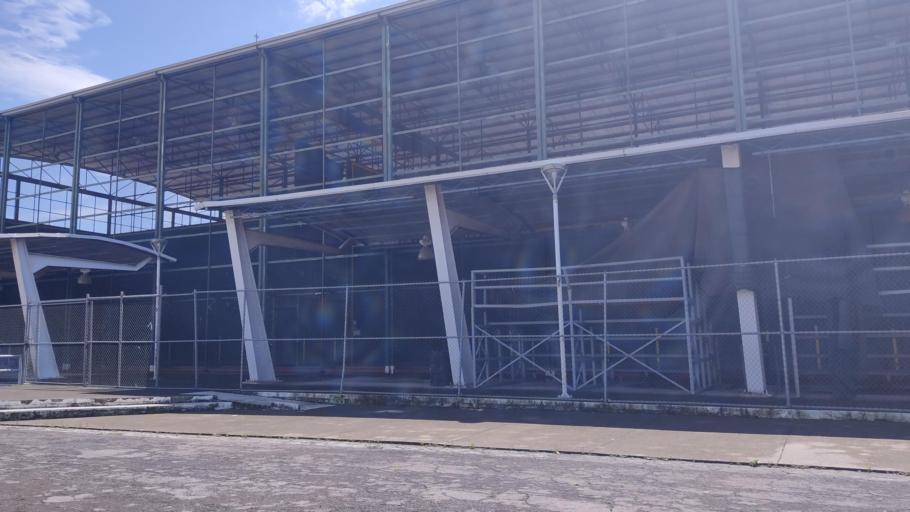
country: MX
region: Nayarit
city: Xalisco
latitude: 21.4754
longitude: -104.8810
